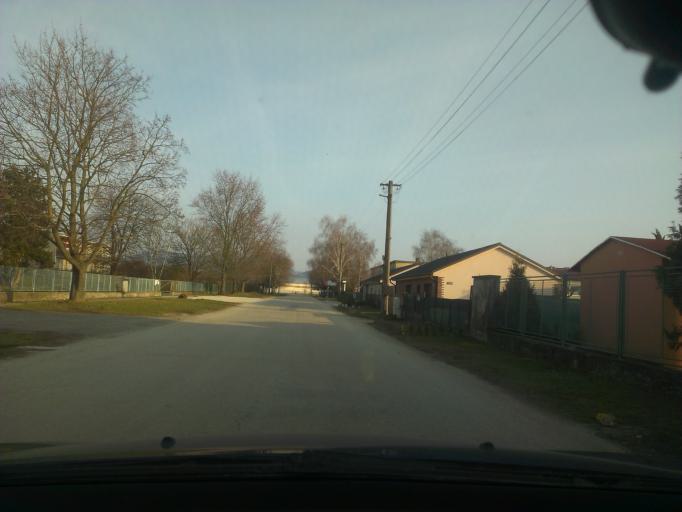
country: SK
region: Trnavsky
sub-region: Okres Trnava
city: Piestany
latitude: 48.6560
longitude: 17.8485
